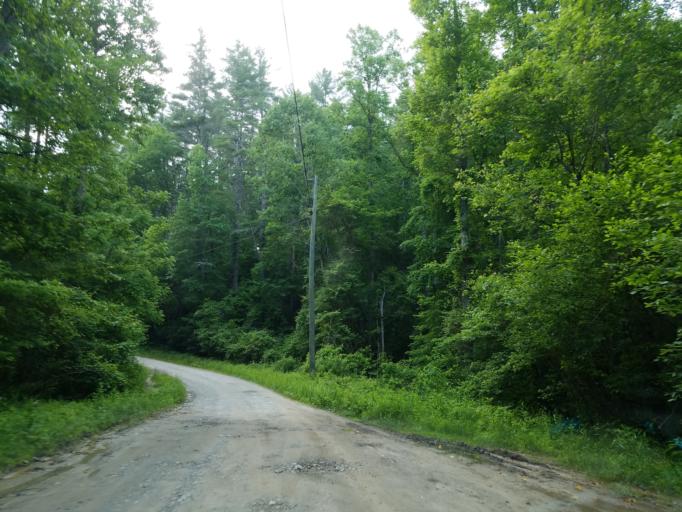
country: US
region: Georgia
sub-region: Lumpkin County
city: Dahlonega
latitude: 34.6008
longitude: -84.0921
